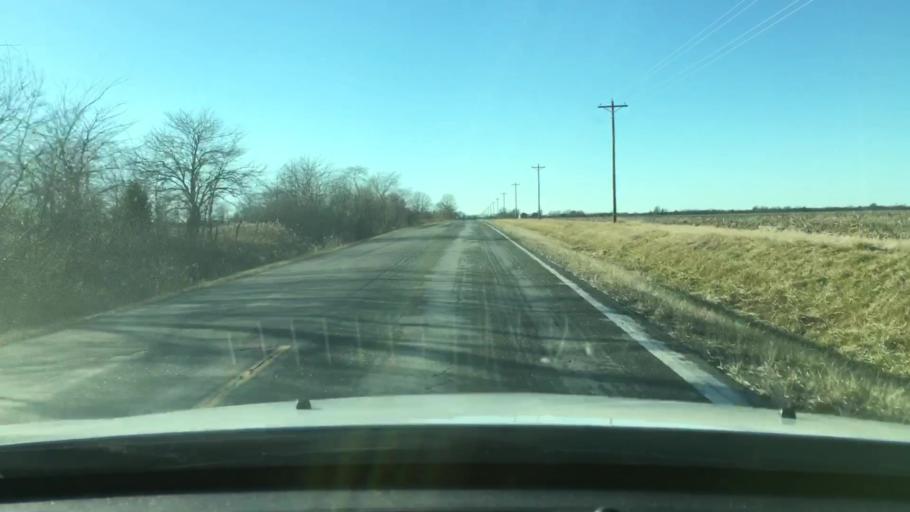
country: US
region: Missouri
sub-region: Audrain County
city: Mexico
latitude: 39.2816
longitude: -91.7237
